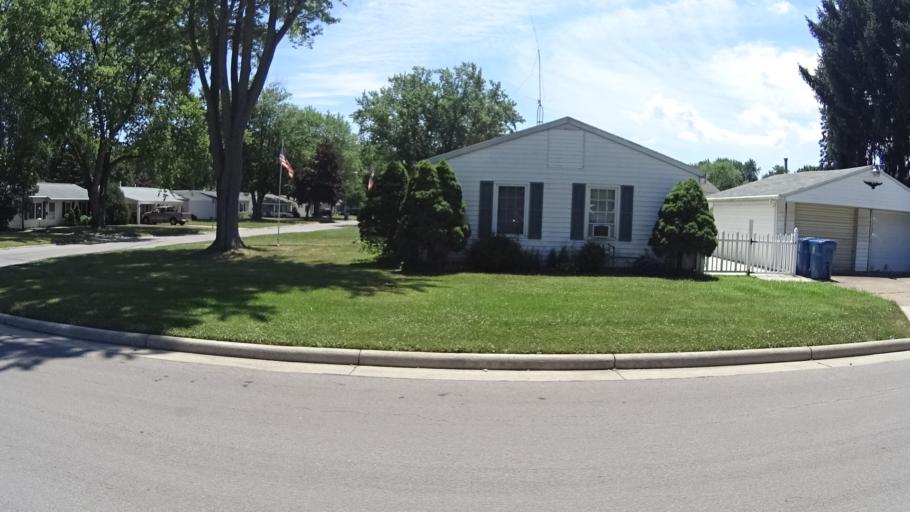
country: US
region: Ohio
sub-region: Erie County
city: Sandusky
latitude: 41.4002
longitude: -82.6749
